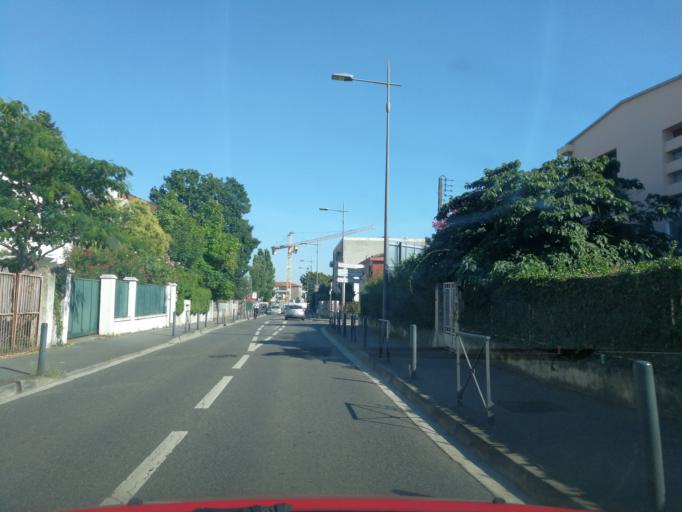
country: FR
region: Midi-Pyrenees
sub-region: Departement de la Haute-Garonne
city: Balma
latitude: 43.6148
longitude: 1.4750
